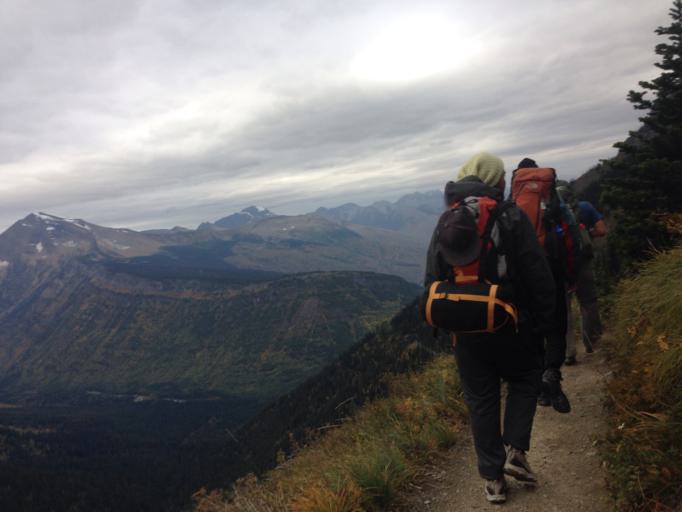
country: US
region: Montana
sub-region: Flathead County
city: Columbia Falls
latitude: 48.7201
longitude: -113.7191
